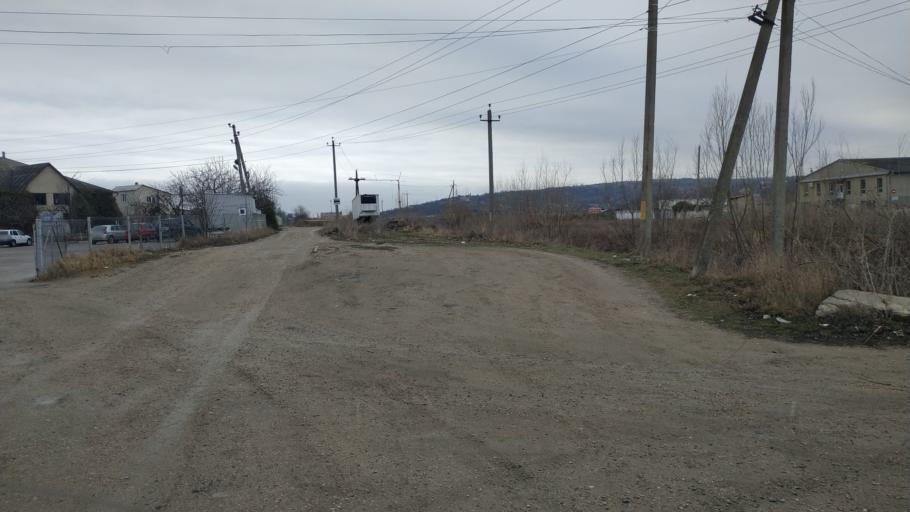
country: MD
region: Laloveni
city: Ialoveni
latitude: 46.9398
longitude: 28.7757
